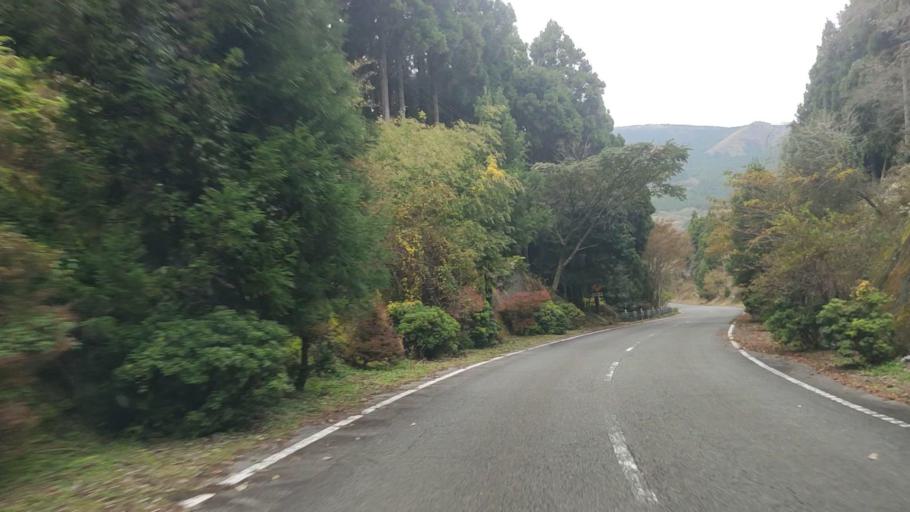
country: JP
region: Shizuoka
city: Heda
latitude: 34.9162
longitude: 138.8424
